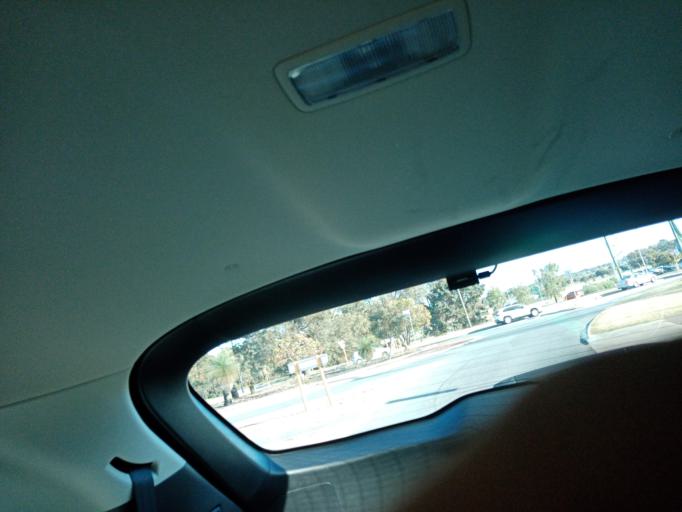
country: AU
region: Western Australia
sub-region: City of Cockburn
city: South Lake
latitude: -32.1186
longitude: 115.8405
